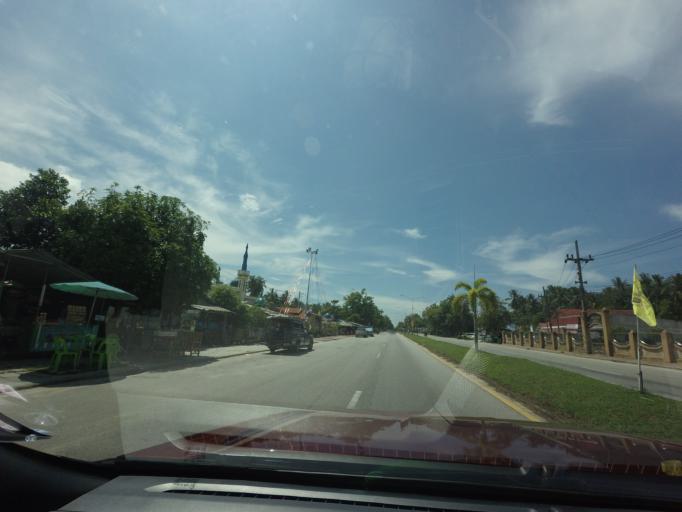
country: TH
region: Pattani
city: Mai Kaen
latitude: 6.6128
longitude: 101.6300
